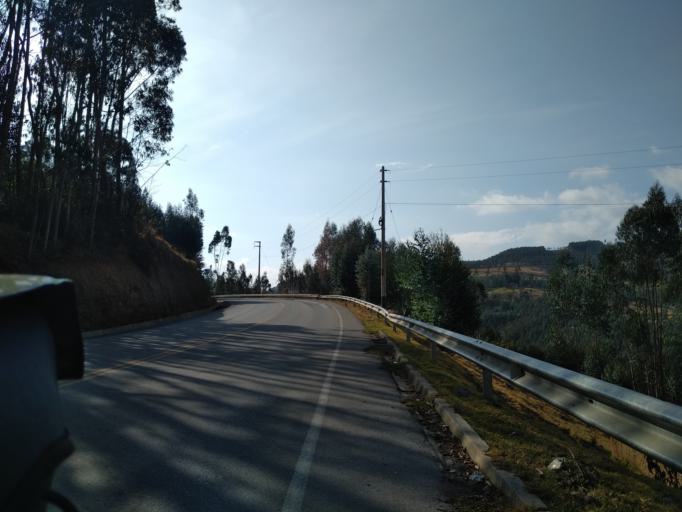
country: PE
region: La Libertad
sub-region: Provincia de Otuzco
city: Agallpampa
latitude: -7.9954
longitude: -78.5142
